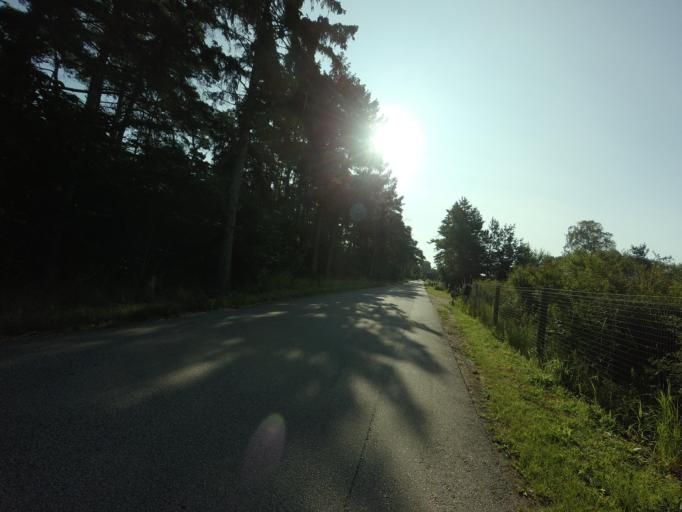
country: SE
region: Skane
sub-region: Kavlinge Kommun
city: Hofterup
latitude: 55.8321
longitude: 12.9556
